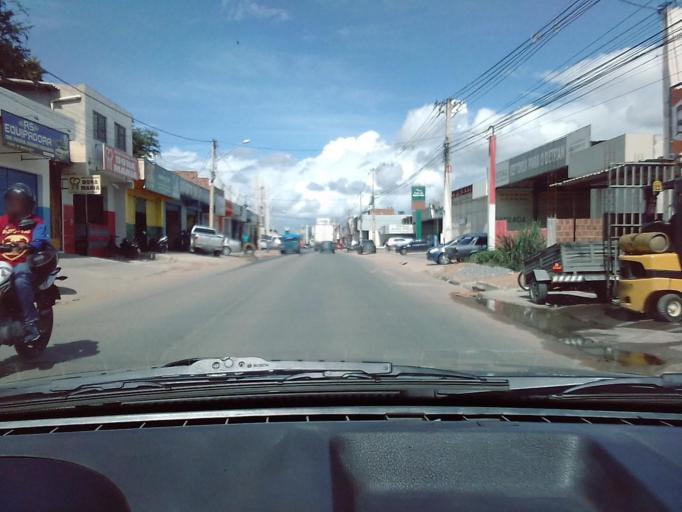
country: BR
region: Pernambuco
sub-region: Vitoria De Santo Antao
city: Vitoria de Santo Antao
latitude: -8.1178
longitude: -35.3017
